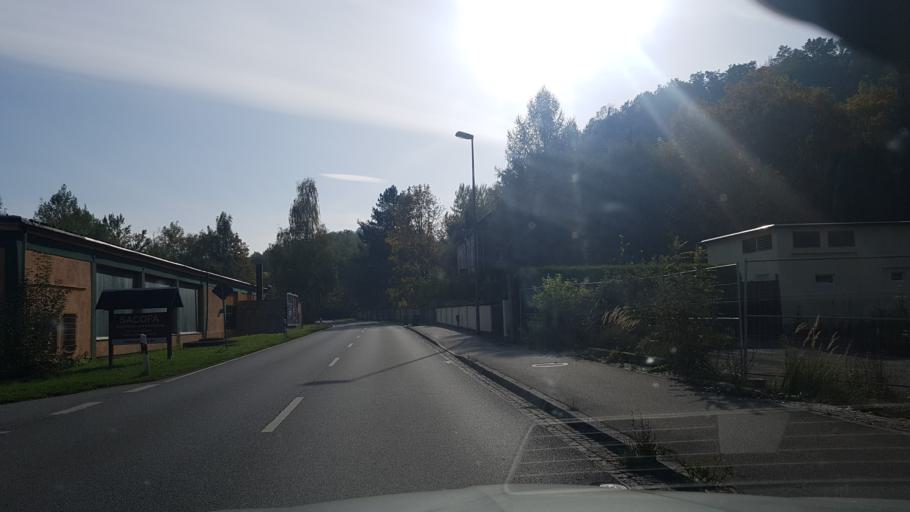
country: DE
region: Saxony
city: Dohma
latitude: 50.9171
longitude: 13.9674
